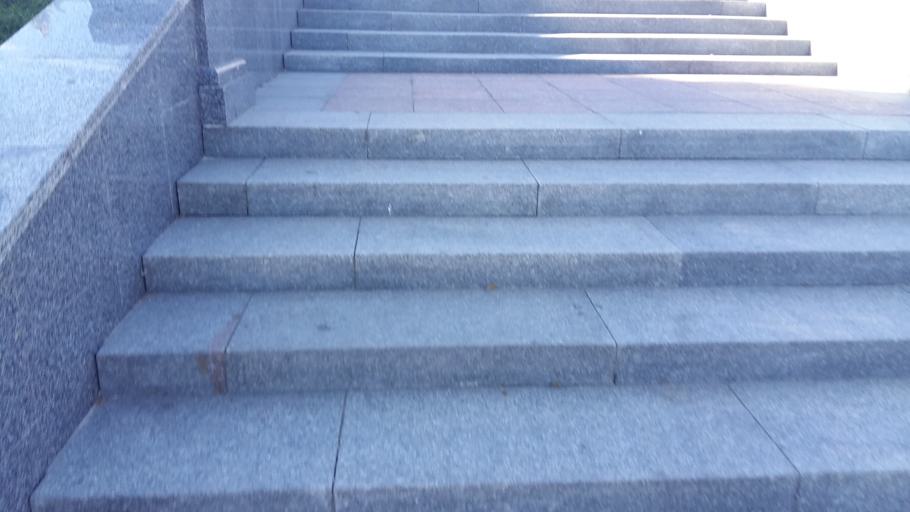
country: BY
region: Grodnenskaya
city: Hrodna
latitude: 53.6745
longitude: 23.8284
